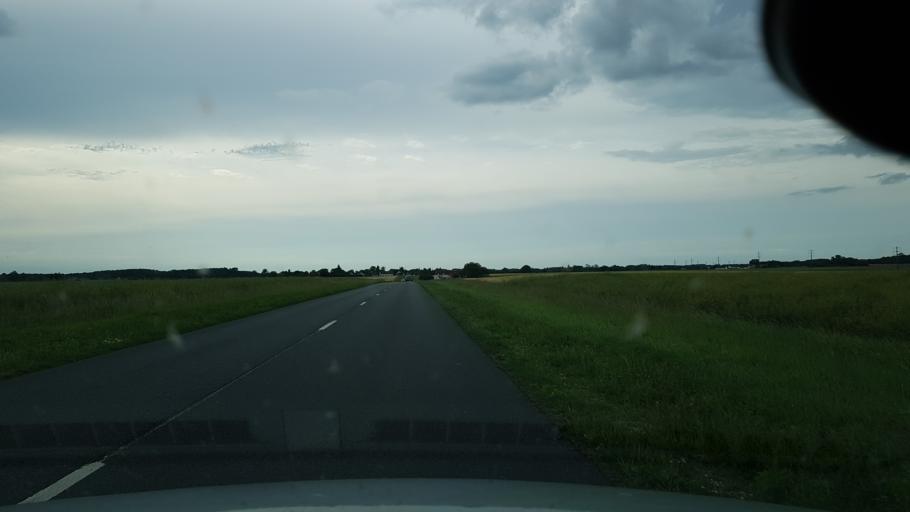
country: FR
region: Centre
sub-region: Departement du Loir-et-Cher
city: Chatillon-sur-Cher
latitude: 47.2963
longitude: 1.5201
